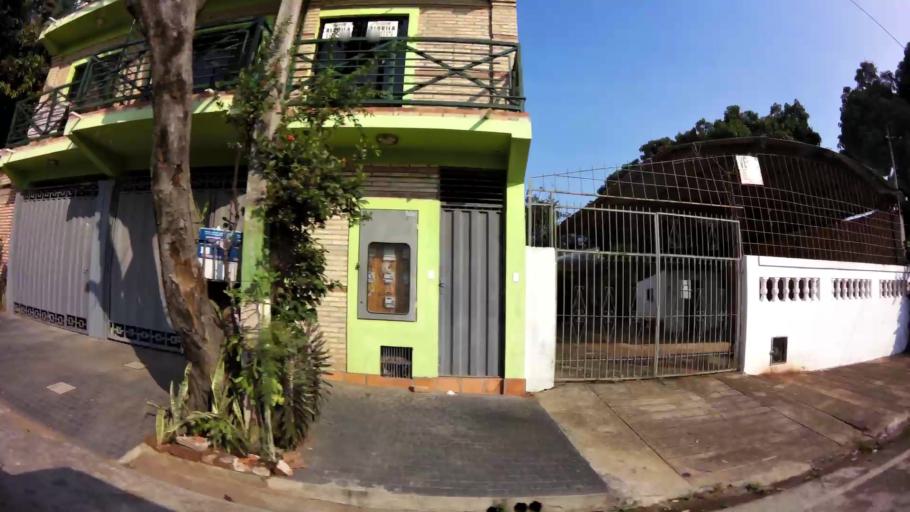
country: PY
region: Central
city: Lambare
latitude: -25.3426
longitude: -57.5852
